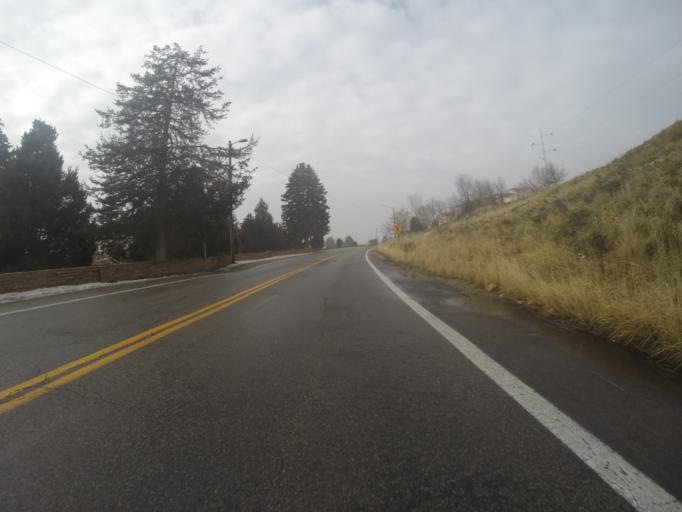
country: US
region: Utah
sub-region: Salt Lake County
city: Salt Lake City
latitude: 40.7797
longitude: -111.8568
